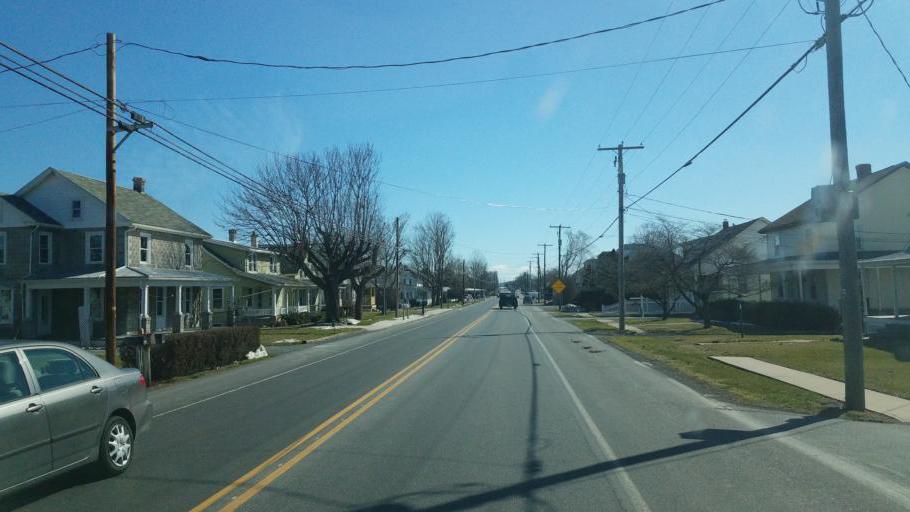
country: US
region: Pennsylvania
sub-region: Lancaster County
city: New Holland
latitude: 40.0917
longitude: -76.1283
